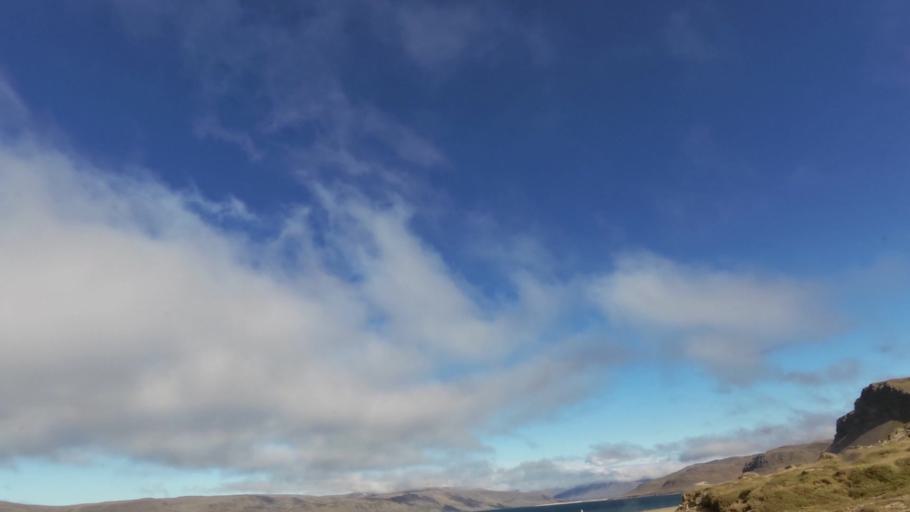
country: IS
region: West
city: Olafsvik
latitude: 65.5765
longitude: -24.0697
